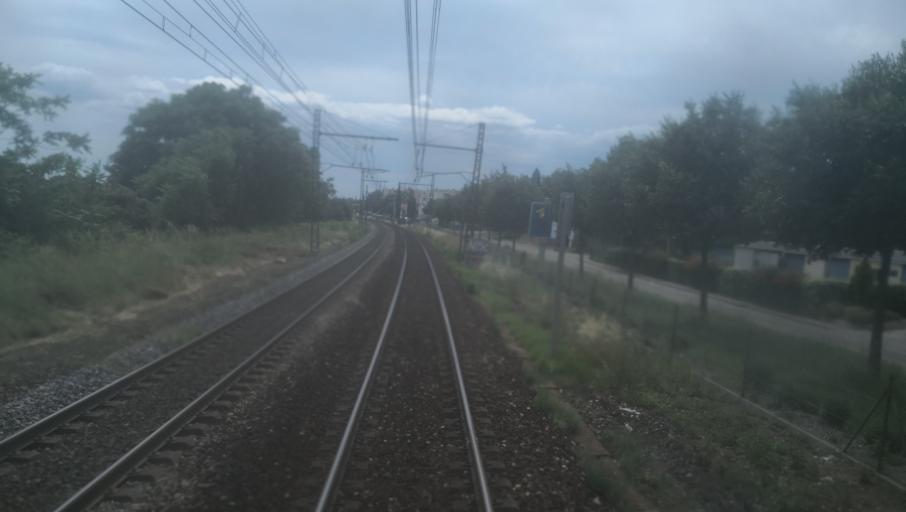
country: FR
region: Languedoc-Roussillon
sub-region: Departement du Gard
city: Nimes
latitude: 43.8219
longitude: 4.3444
